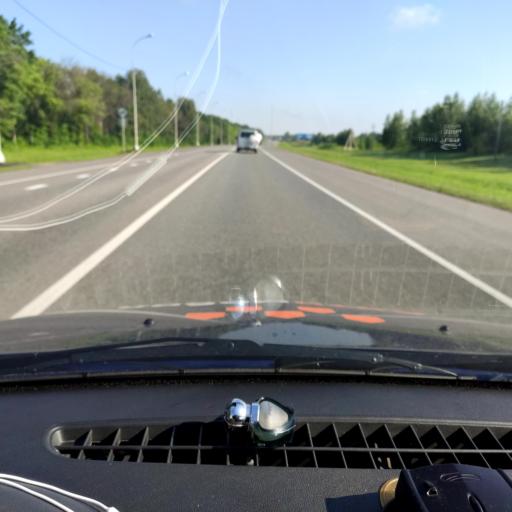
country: RU
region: Orjol
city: Orel
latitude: 52.9051
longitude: 36.1552
